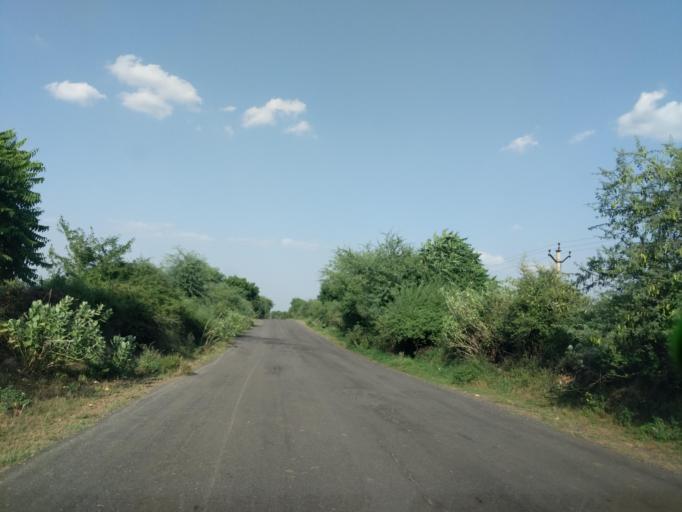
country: IN
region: Rajasthan
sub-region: Churu
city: Rajgarh
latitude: 28.4963
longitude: 75.3763
